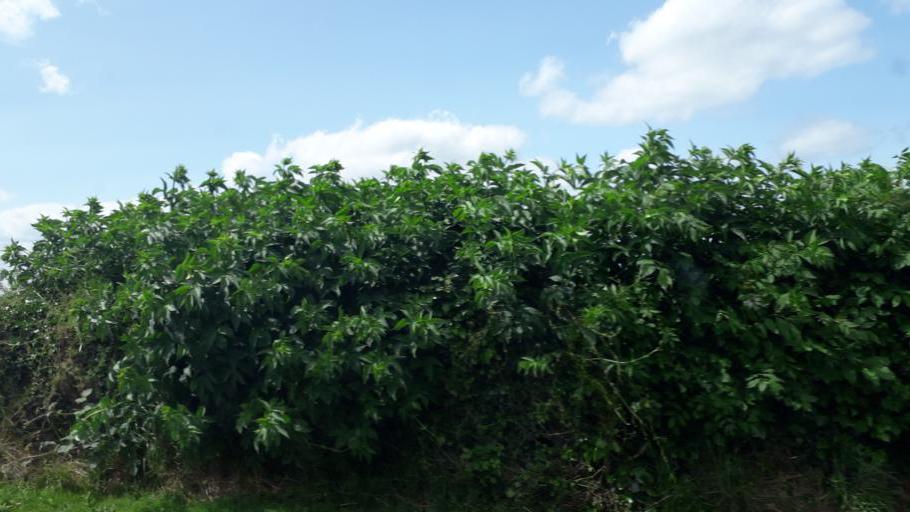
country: IE
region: Leinster
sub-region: Kildare
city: Moone
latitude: 53.0171
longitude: -6.8021
